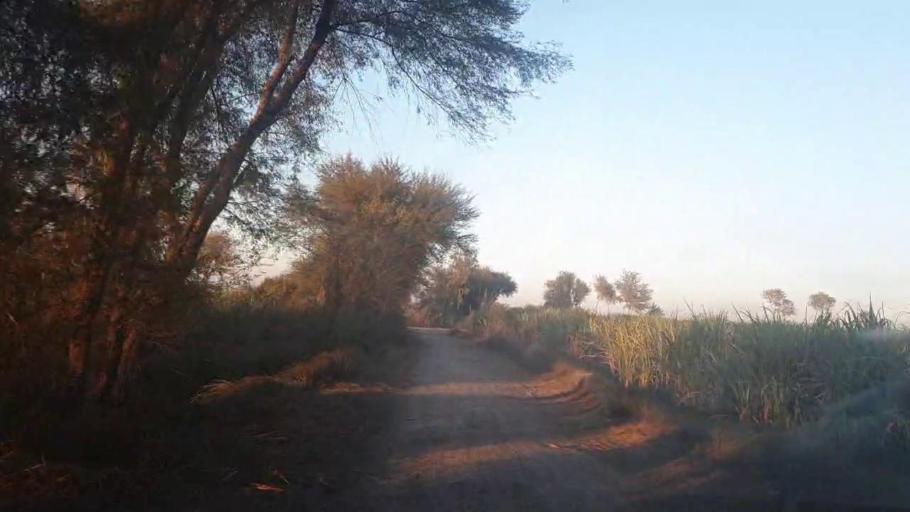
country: PK
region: Sindh
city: Ghotki
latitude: 28.0307
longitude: 69.2941
